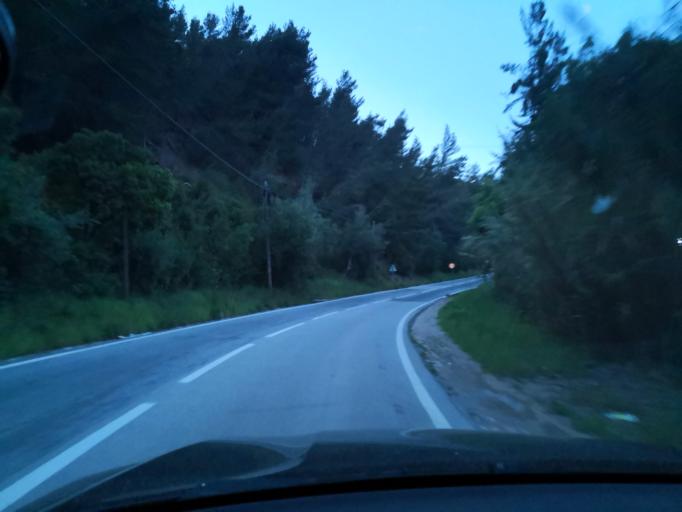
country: PT
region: Setubal
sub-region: Setubal
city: Setubal
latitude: 38.5024
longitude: -8.9294
